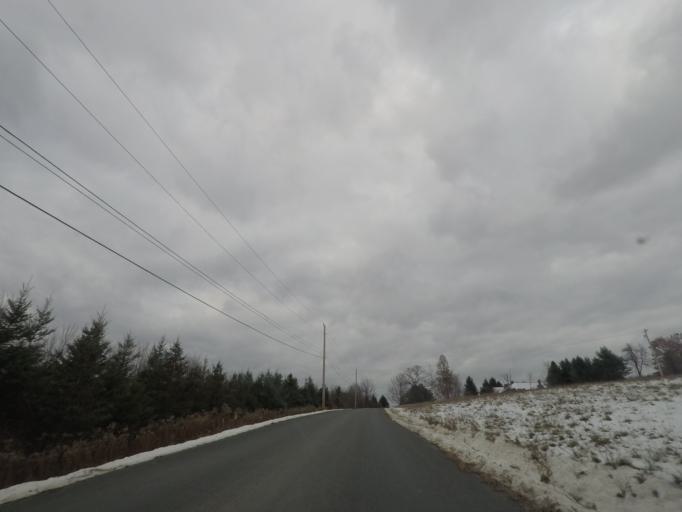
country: US
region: New York
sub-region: Rensselaer County
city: West Sand Lake
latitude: 42.5957
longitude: -73.6310
